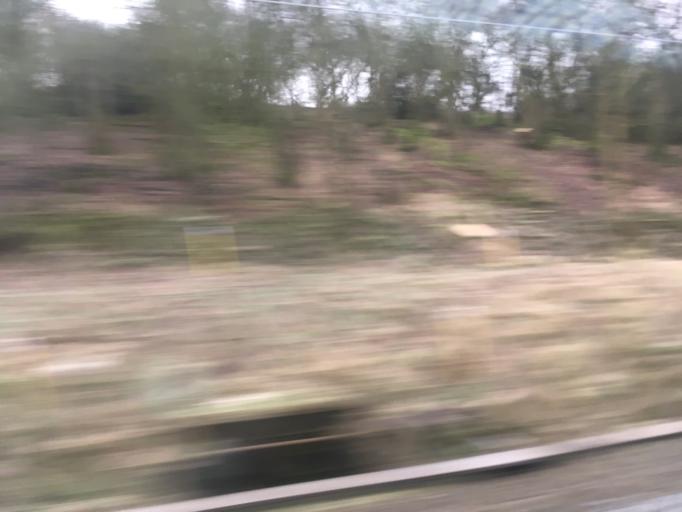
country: GB
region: England
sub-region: Wiltshire
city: Lydiard Tregoze
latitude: 51.5376
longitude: -1.8623
